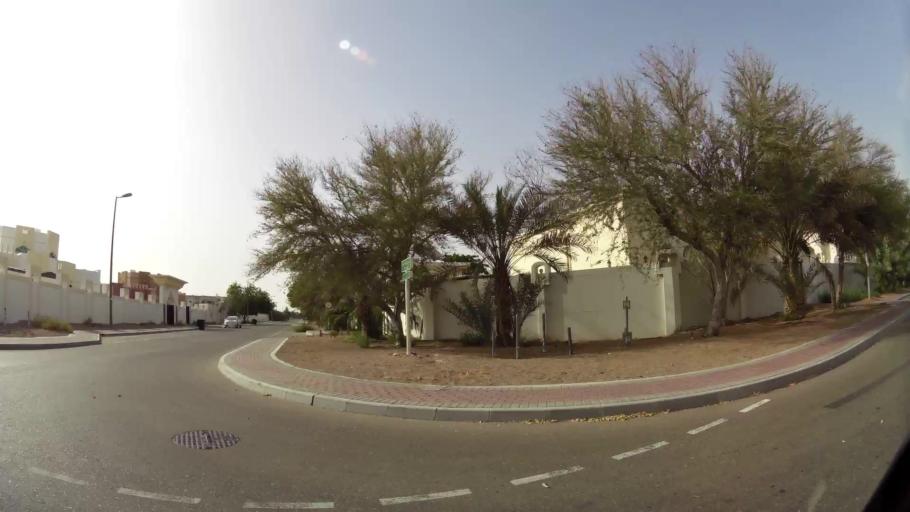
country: AE
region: Abu Dhabi
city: Al Ain
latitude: 24.1999
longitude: 55.6136
